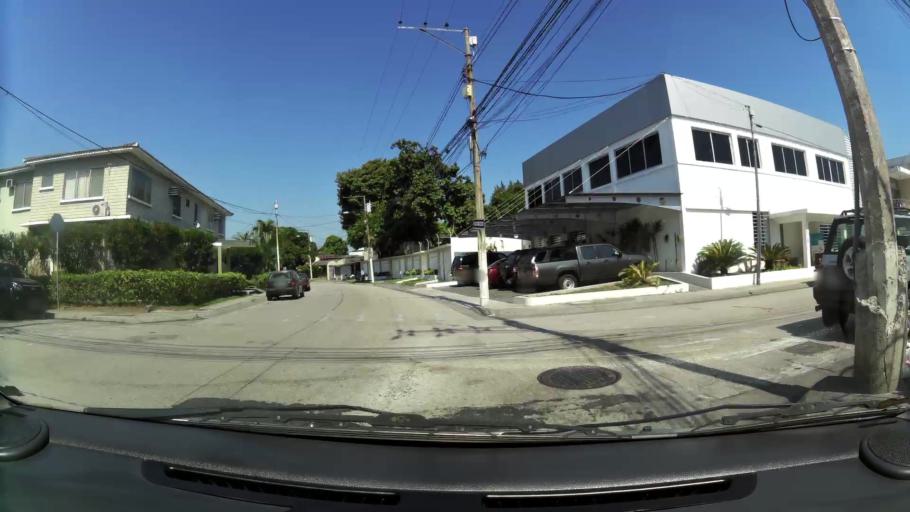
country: EC
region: Guayas
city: Guayaquil
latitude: -2.1744
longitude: -79.9077
